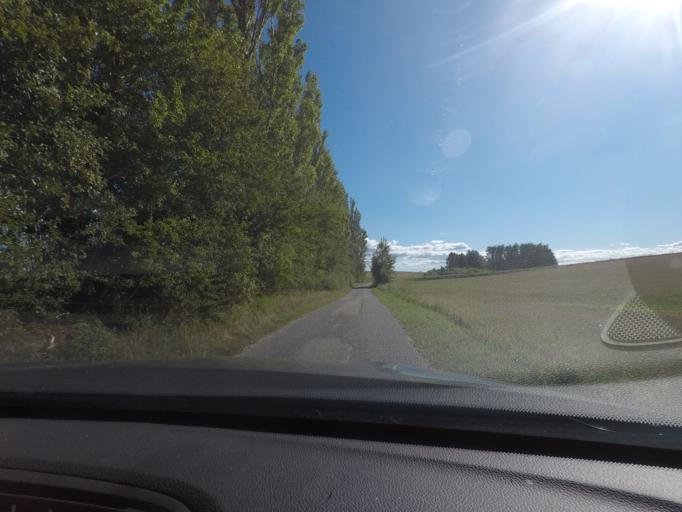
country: DK
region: Zealand
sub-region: Guldborgsund Kommune
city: Sakskobing
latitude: 54.9773
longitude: 11.5487
